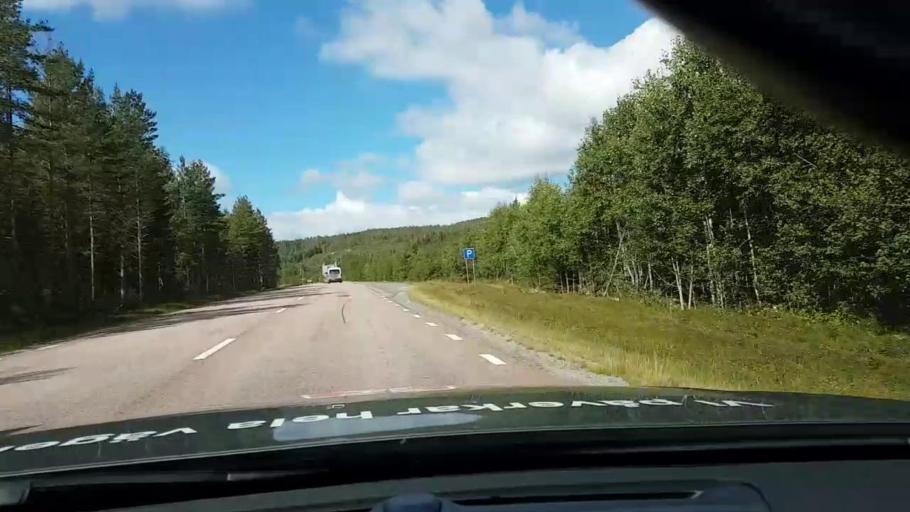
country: SE
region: Vaesternorrland
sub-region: OErnskoeldsviks Kommun
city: Bjasta
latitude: 63.3779
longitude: 18.4225
